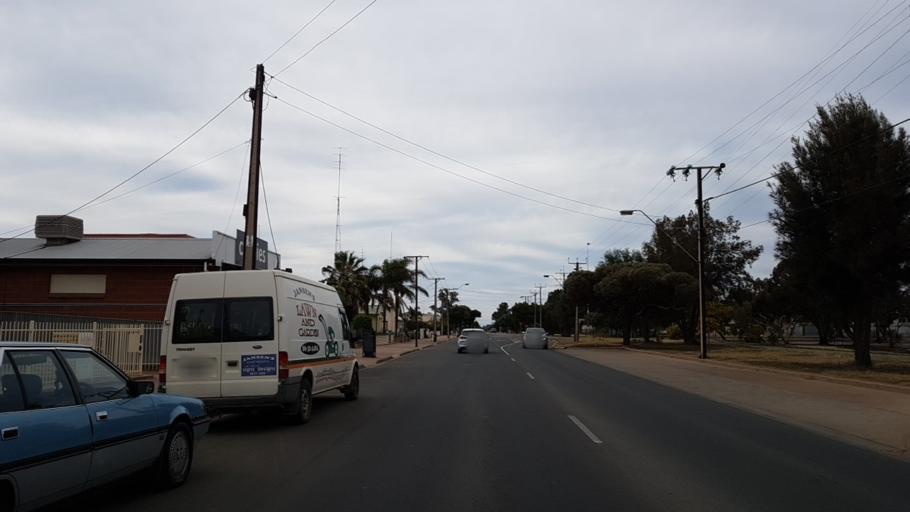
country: AU
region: South Australia
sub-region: Port Pirie City and Dists
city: Port Pirie
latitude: -33.1848
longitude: 138.0039
